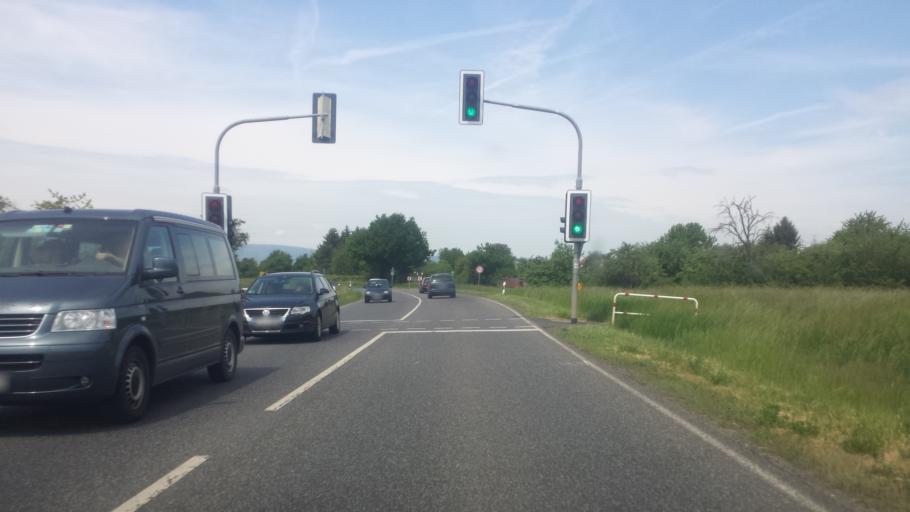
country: DE
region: Hesse
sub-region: Regierungsbezirk Darmstadt
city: Bad Vilbel
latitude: 50.1959
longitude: 8.7205
